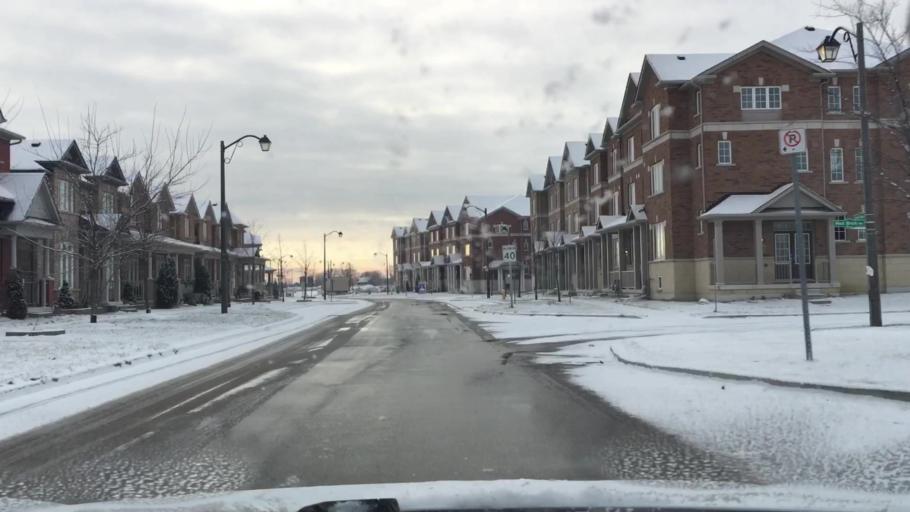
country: CA
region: Ontario
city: Markham
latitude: 43.8867
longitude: -79.2186
